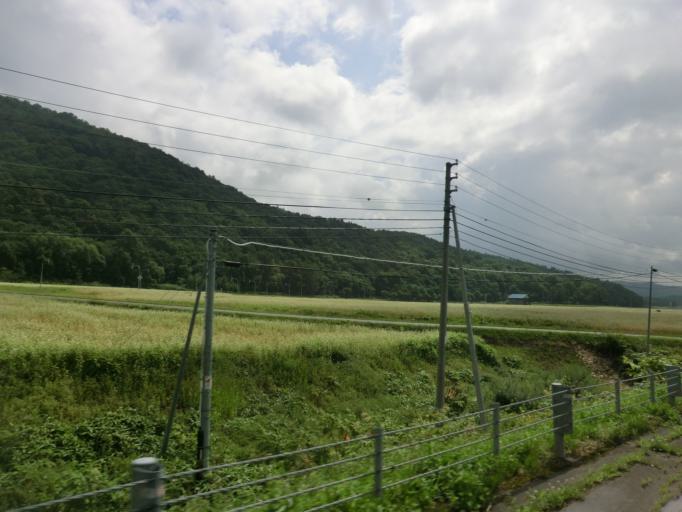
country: JP
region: Hokkaido
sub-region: Asahikawa-shi
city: Asahikawa
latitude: 44.0518
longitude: 142.1438
